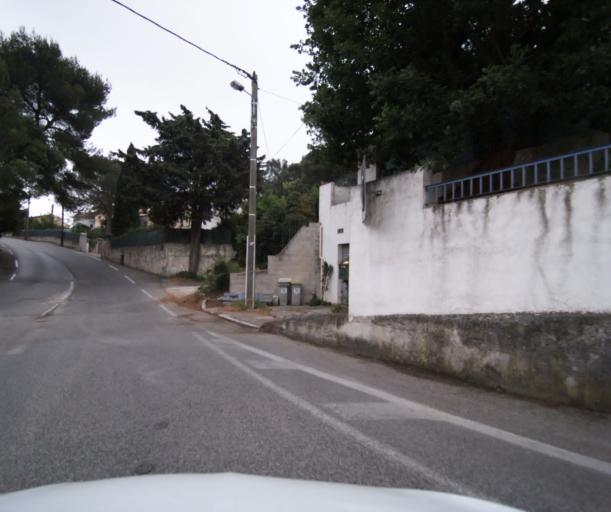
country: FR
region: Provence-Alpes-Cote d'Azur
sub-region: Departement du Var
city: La Seyne-sur-Mer
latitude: 43.0901
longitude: 5.8750
